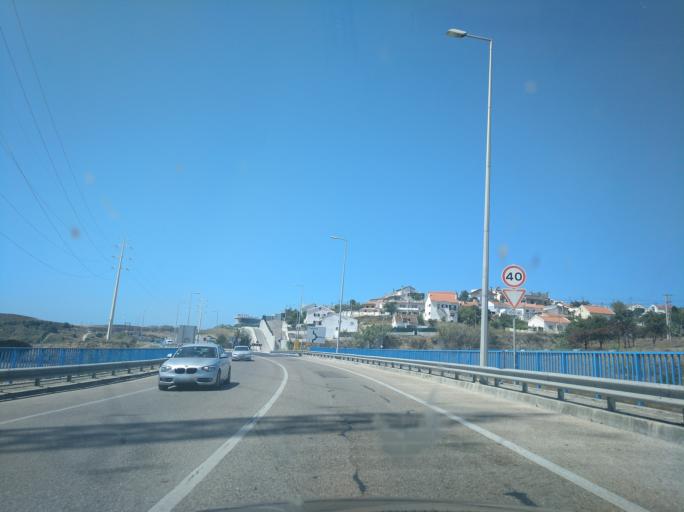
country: PT
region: Setubal
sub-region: Almada
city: Caparica
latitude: 38.6562
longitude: -9.2175
